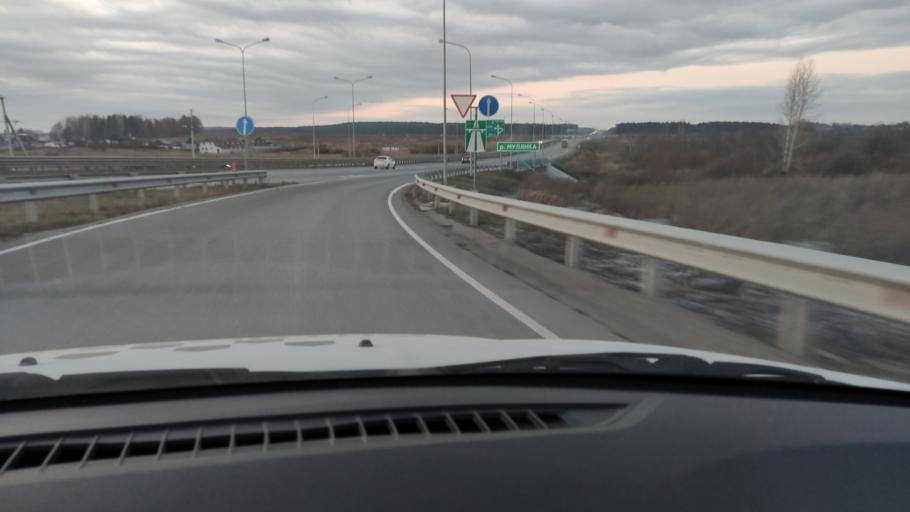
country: RU
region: Perm
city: Lobanovo
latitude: 57.8025
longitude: 56.3253
